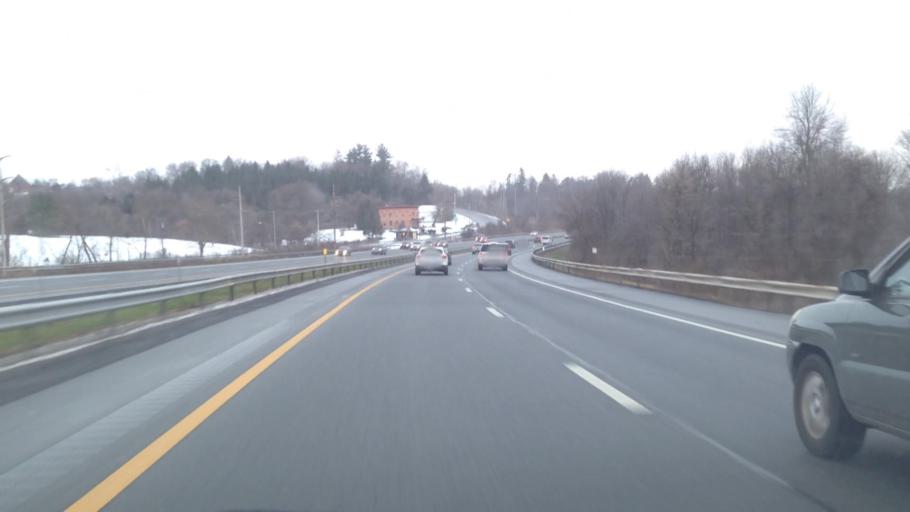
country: US
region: New York
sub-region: Montgomery County
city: Fort Plain
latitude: 42.9406
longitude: -74.6273
